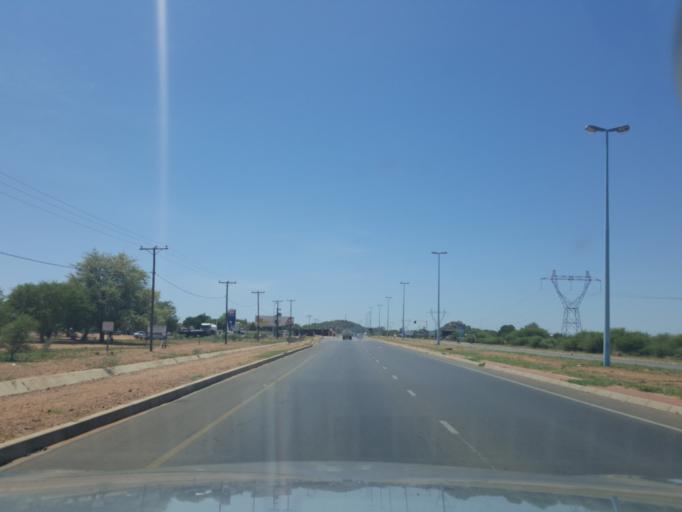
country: BW
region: Kweneng
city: Gaphatshwe
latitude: -24.5866
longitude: 25.8428
